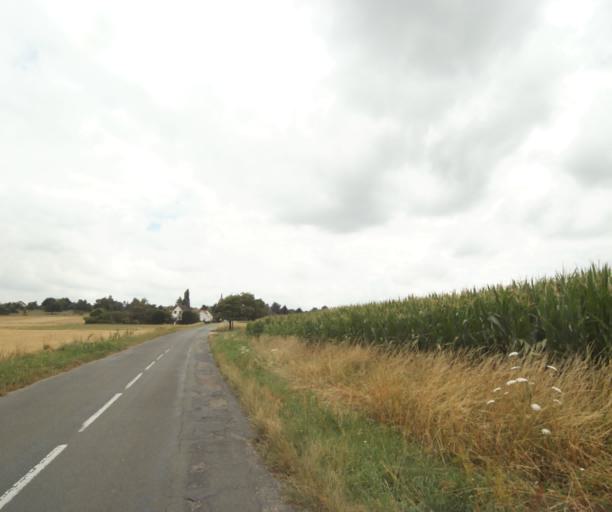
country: FR
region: Centre
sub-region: Departement du Loiret
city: Mardie
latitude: 47.8817
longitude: 2.0523
